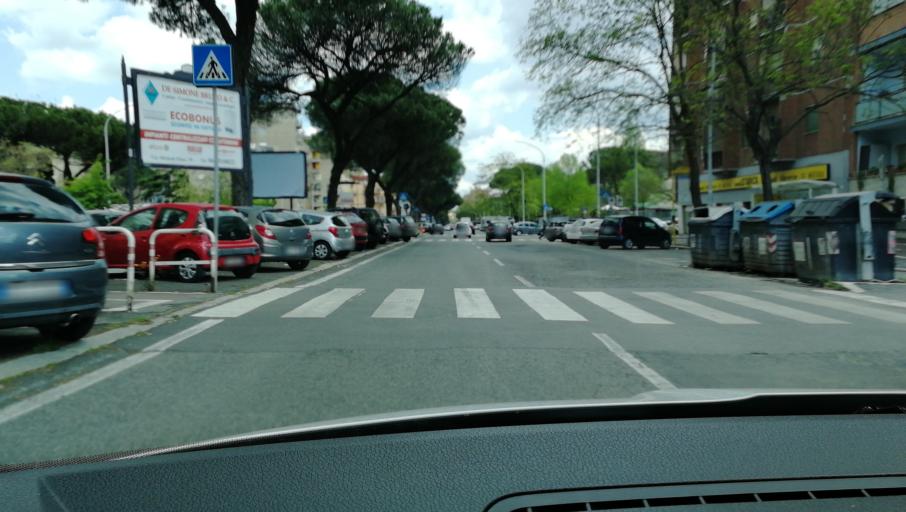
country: IT
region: Latium
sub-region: Citta metropolitana di Roma Capitale
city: Rome
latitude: 41.8458
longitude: 12.4855
